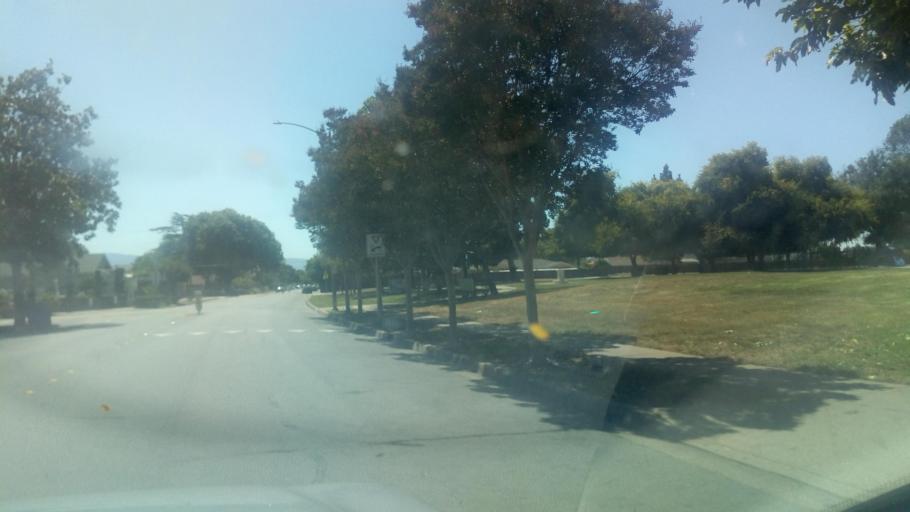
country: US
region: California
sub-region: Santa Clara County
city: Milpitas
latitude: 37.4564
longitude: -121.9020
